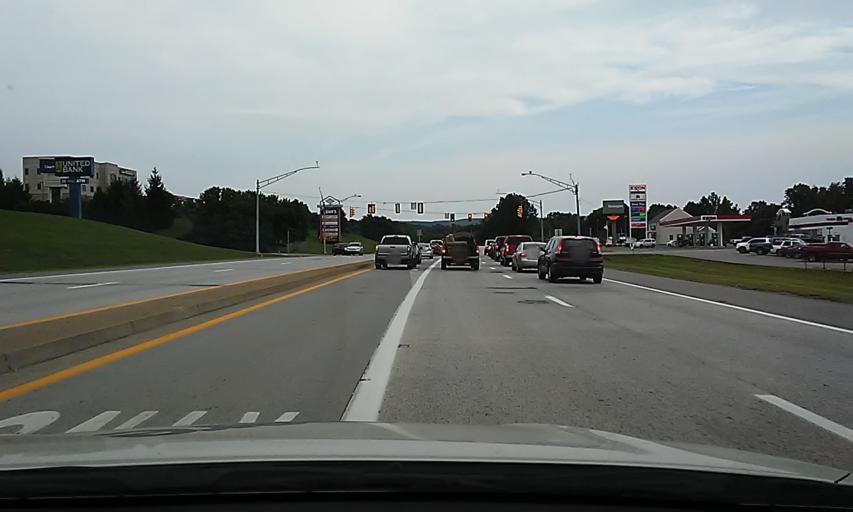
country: US
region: West Virginia
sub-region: Monongalia County
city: Brookhaven
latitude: 39.6491
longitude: -79.9023
